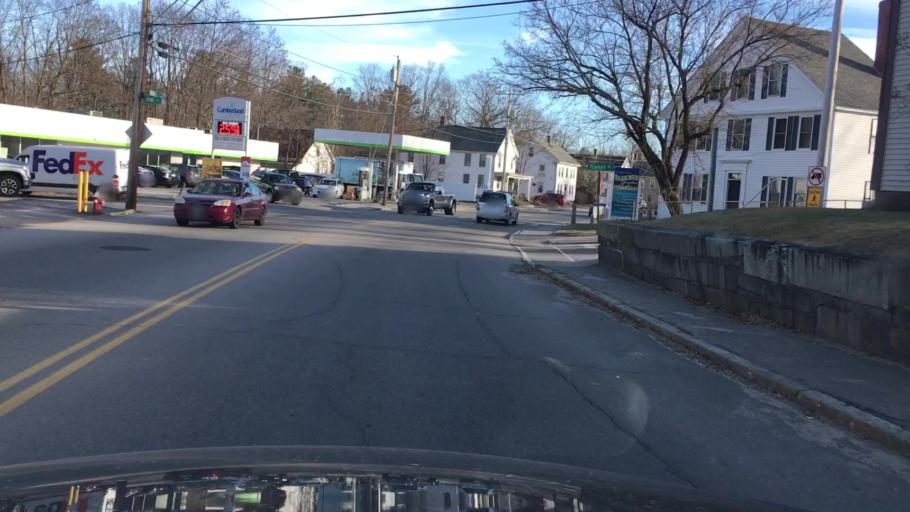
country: US
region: New Hampshire
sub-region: Hillsborough County
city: Milford
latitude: 42.8355
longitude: -71.6472
